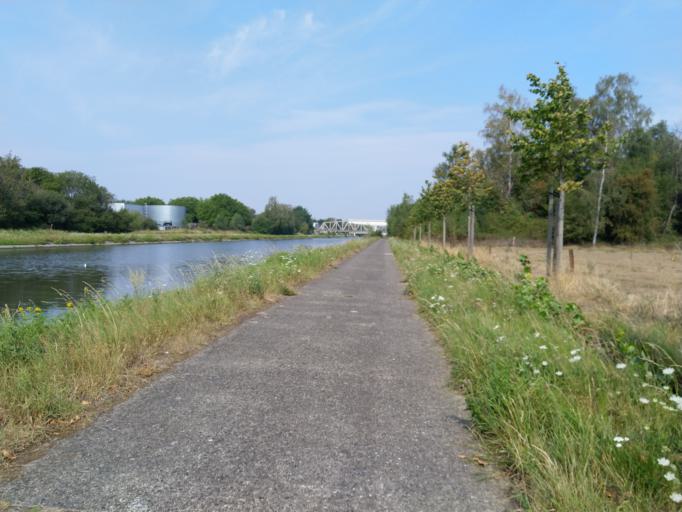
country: BE
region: Wallonia
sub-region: Province du Hainaut
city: Seneffe
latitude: 50.5160
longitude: 4.2585
